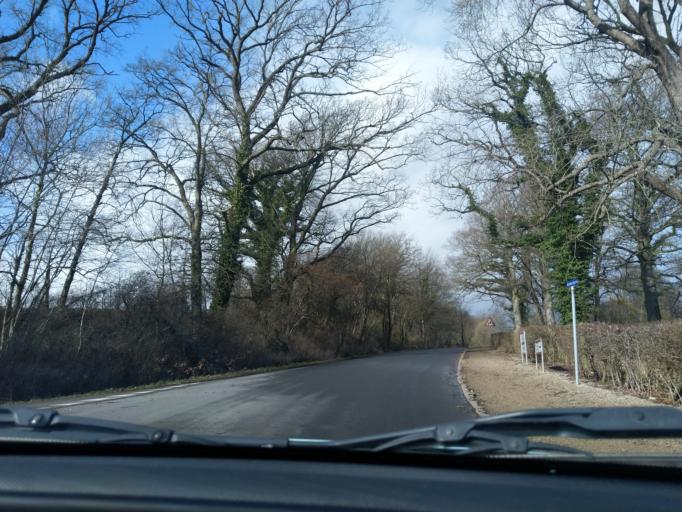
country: DK
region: Zealand
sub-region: Naestved Kommune
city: Naestved
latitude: 55.3124
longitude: 11.6721
